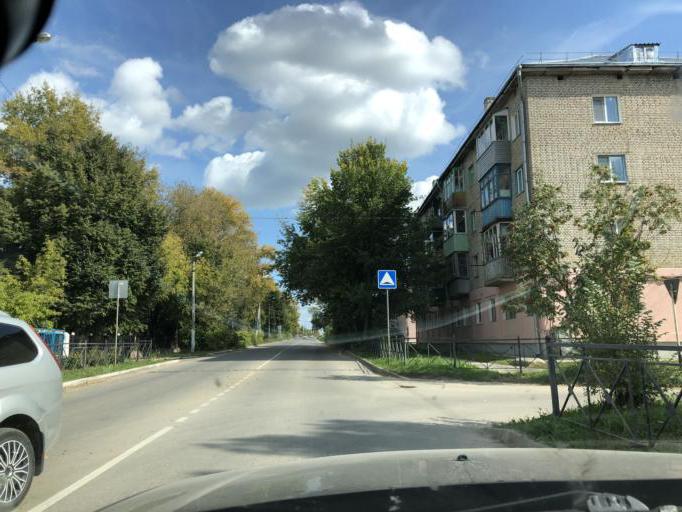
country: RU
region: Tula
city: Yasnogorsk
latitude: 54.4823
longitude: 37.6952
